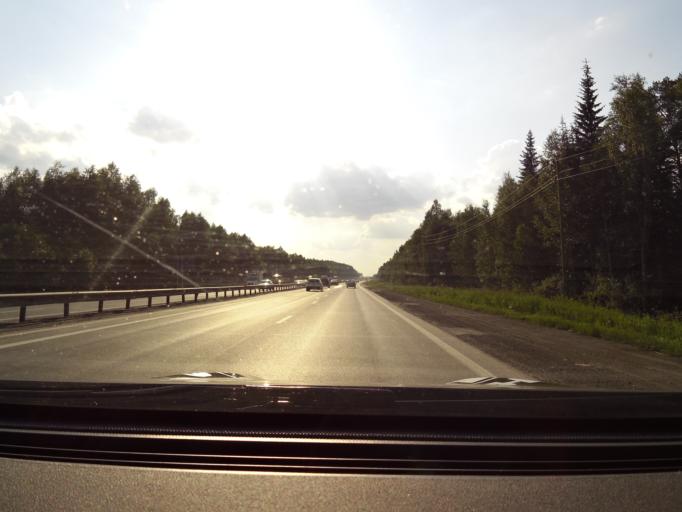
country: RU
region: Sverdlovsk
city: Severka
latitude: 56.8358
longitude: 60.2875
